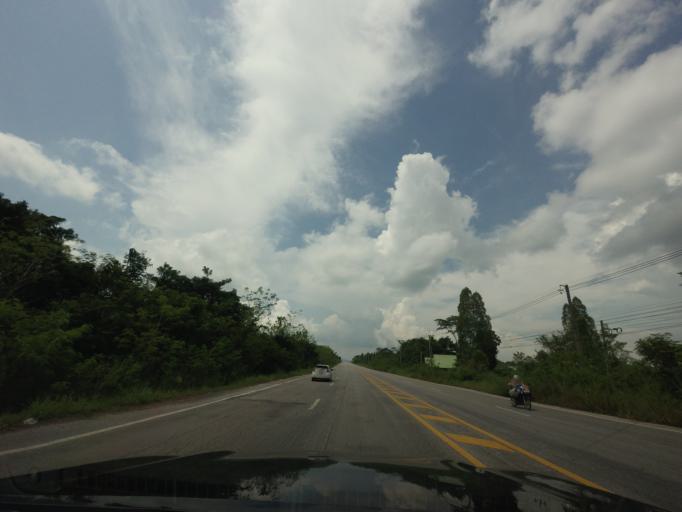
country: TH
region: Khon Kaen
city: Phu Wiang
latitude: 16.6801
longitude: 102.3474
